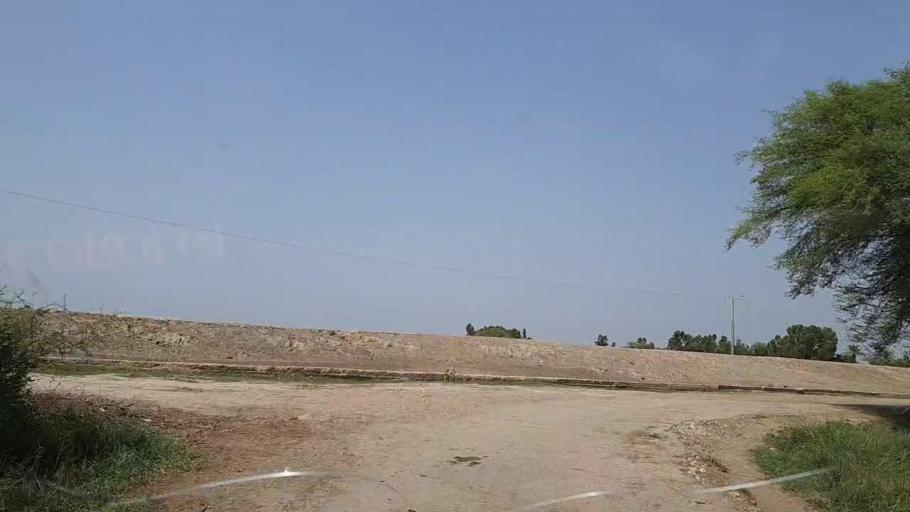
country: PK
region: Sindh
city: Ghotki
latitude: 28.0725
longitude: 69.3180
